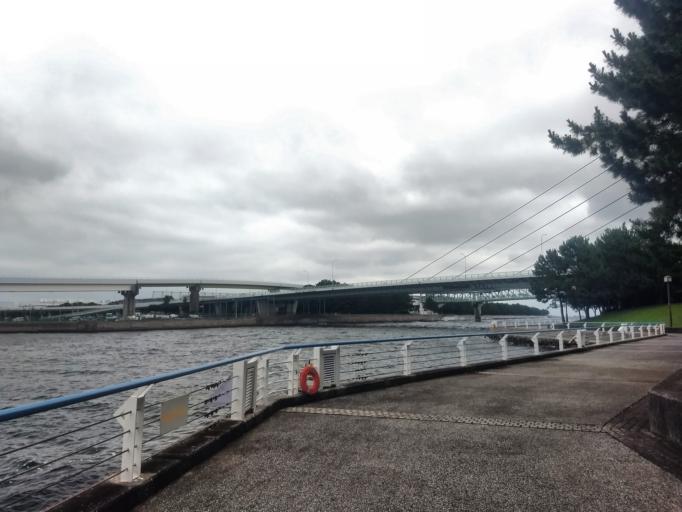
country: JP
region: Kanagawa
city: Yokosuka
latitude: 35.3385
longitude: 139.6430
